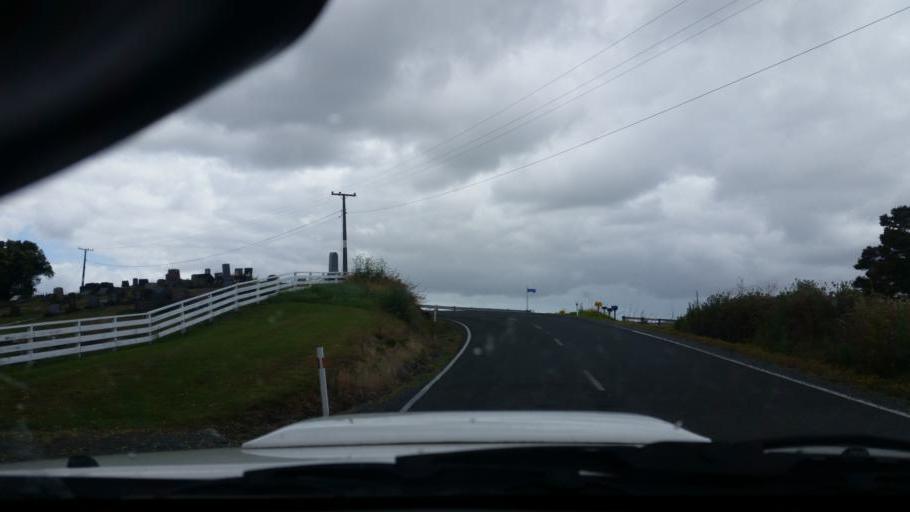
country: NZ
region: Northland
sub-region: Whangarei
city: Ruakaka
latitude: -36.1030
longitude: 174.3507
